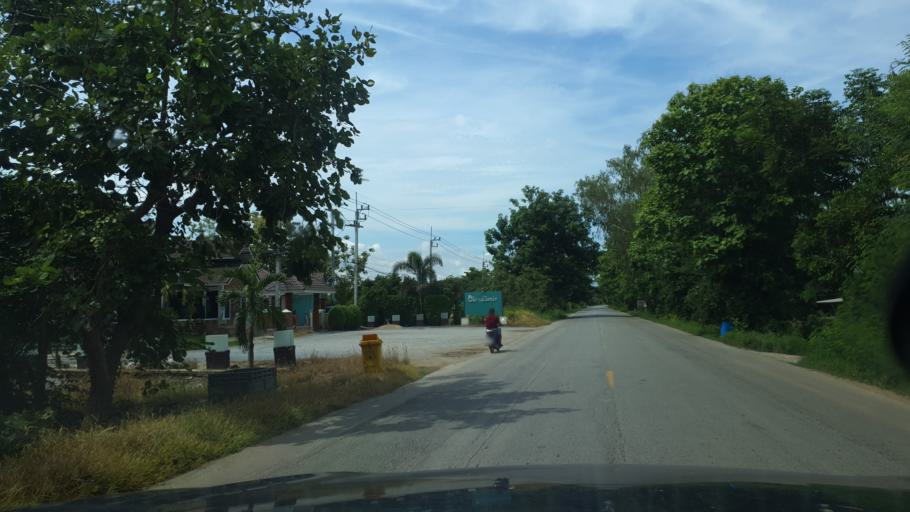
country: TH
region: Sukhothai
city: Sukhothai
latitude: 17.0659
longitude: 99.8301
